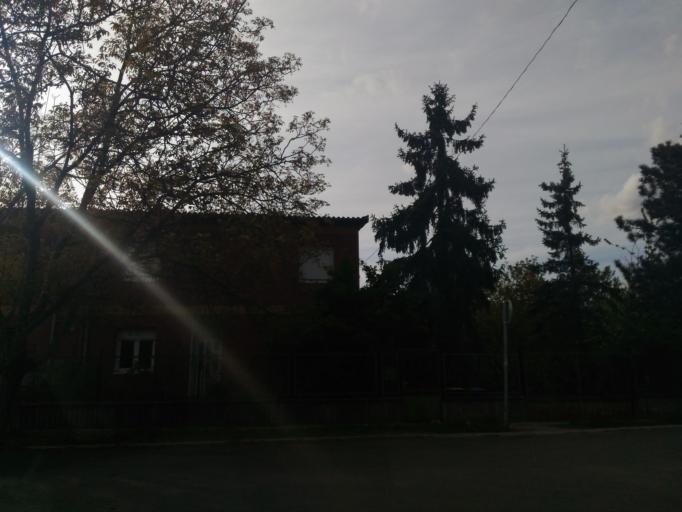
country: HU
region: Budapest
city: Budapest XXII. keruelet
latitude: 47.4239
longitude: 19.0288
